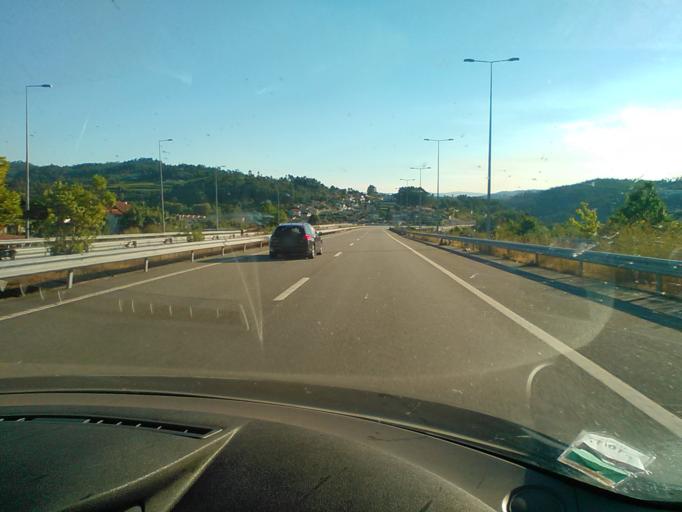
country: PT
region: Braga
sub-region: Fafe
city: Fafe
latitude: 41.4403
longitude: -8.1621
